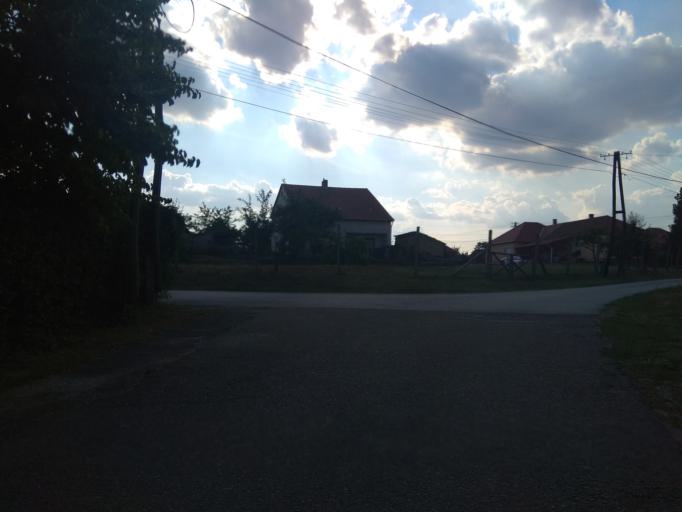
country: HU
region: Borsod-Abauj-Zemplen
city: Mezokeresztes
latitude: 47.8858
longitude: 20.6864
